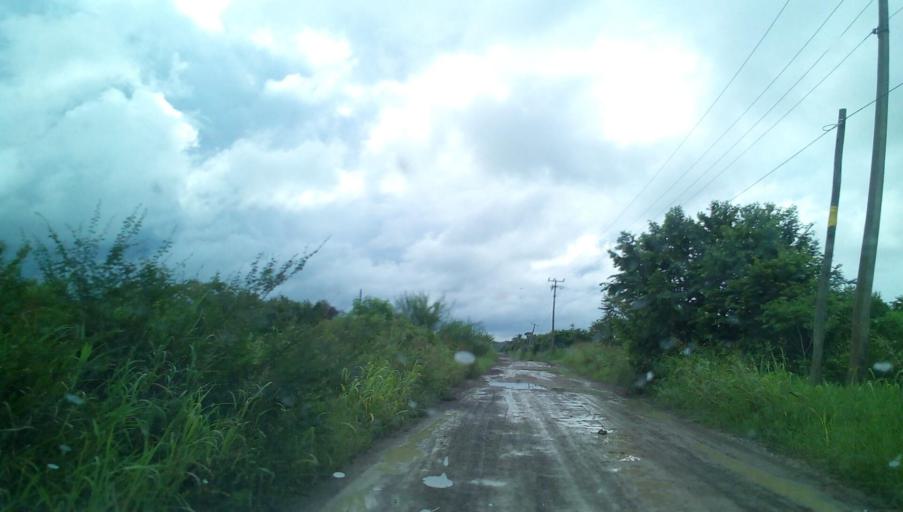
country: MX
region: Veracruz
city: Panuco
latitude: 21.8483
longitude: -98.1405
